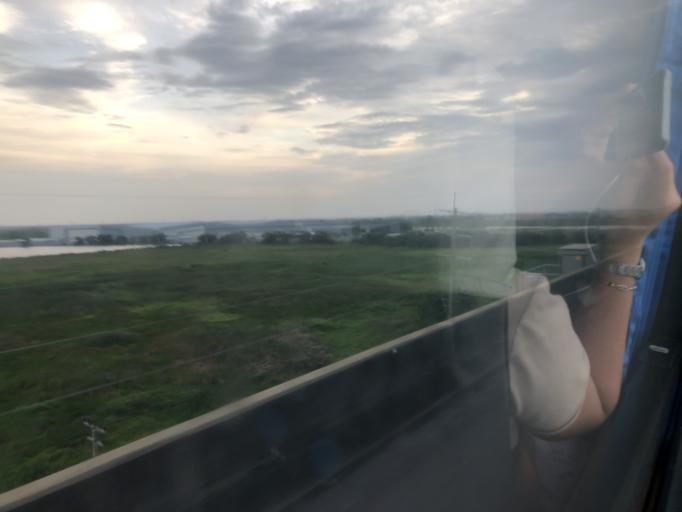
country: TH
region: Samut Prakan
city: Bang Bo
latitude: 13.5801
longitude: 100.8737
